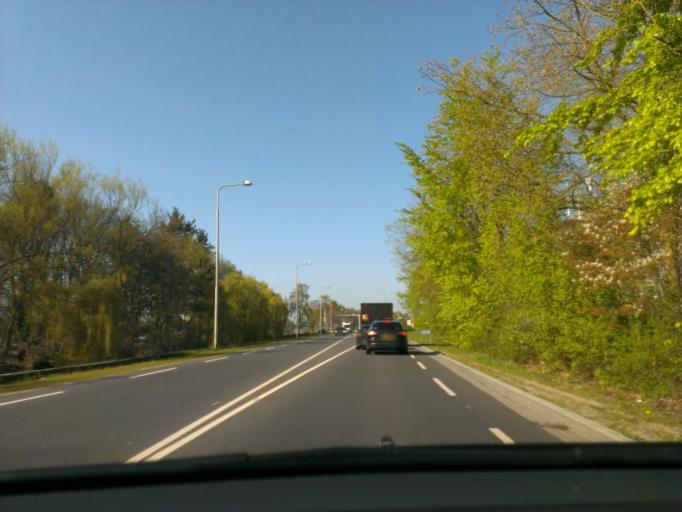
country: NL
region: Gelderland
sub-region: Gemeente Apeldoorn
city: Apeldoorn
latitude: 52.2336
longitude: 5.9758
